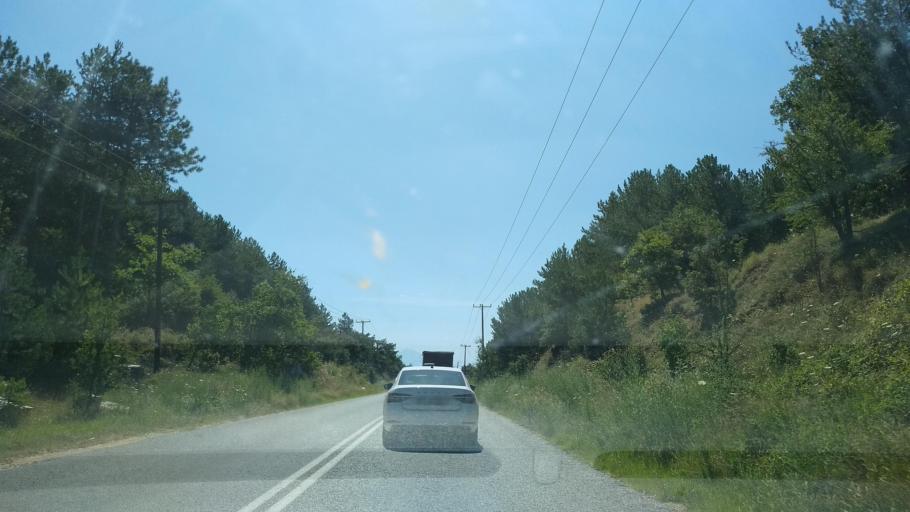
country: GR
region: Central Macedonia
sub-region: Nomos Chalkidikis
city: Megali Panagia
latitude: 40.4462
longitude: 23.6697
